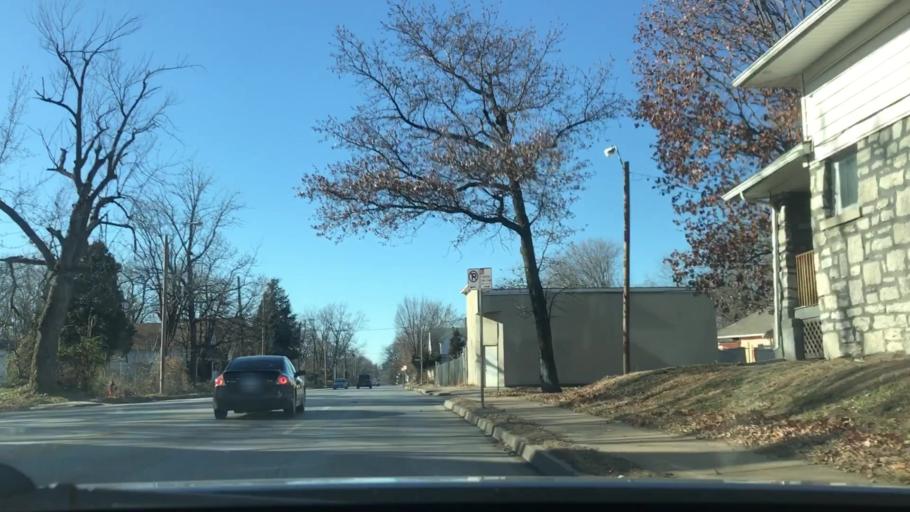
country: US
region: Missouri
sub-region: Jackson County
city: Kansas City
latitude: 39.0834
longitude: -94.5219
